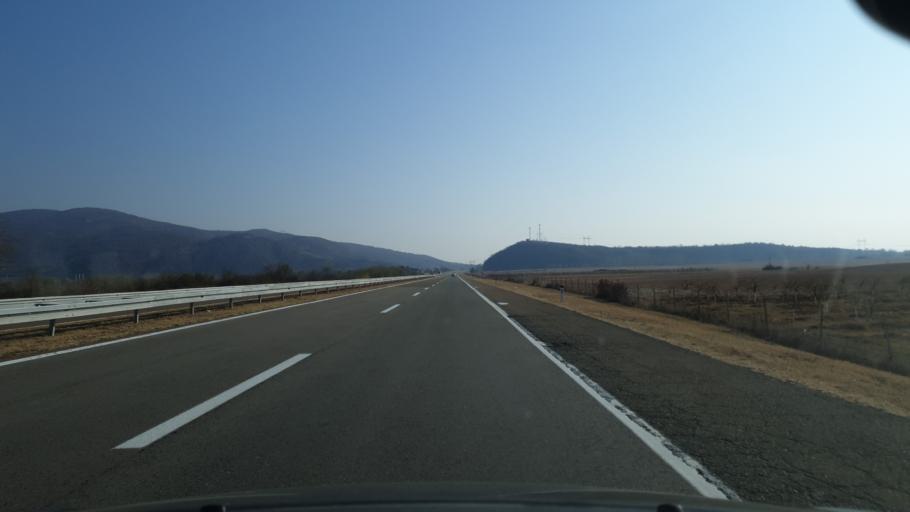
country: RS
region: Central Serbia
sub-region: Nisavski Okrug
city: Doljevac
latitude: 43.2333
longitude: 21.8232
